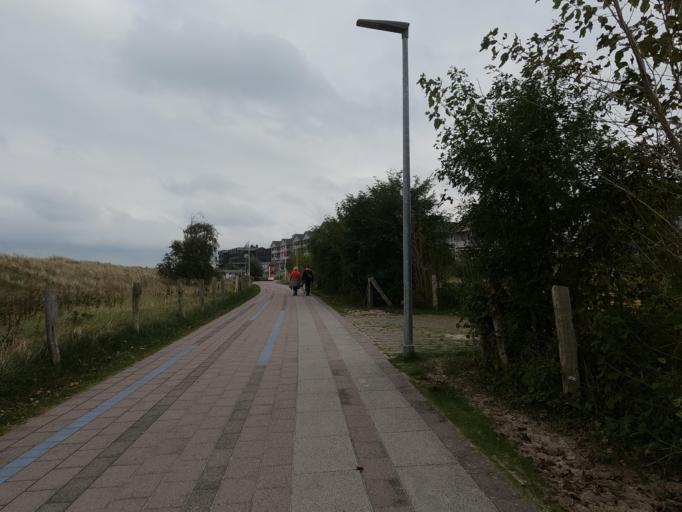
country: DE
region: Schleswig-Holstein
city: Heiligenhafen
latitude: 54.3805
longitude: 10.9757
